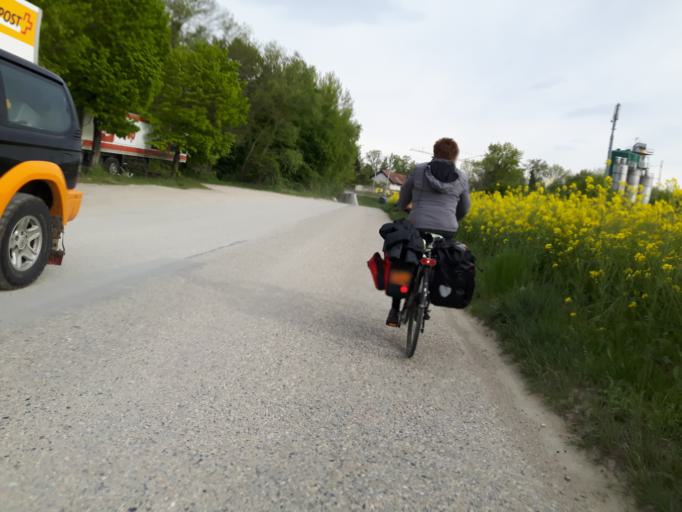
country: CH
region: Vaud
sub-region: Jura-Nord vaudois District
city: Grandson
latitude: 46.8259
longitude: 6.6776
